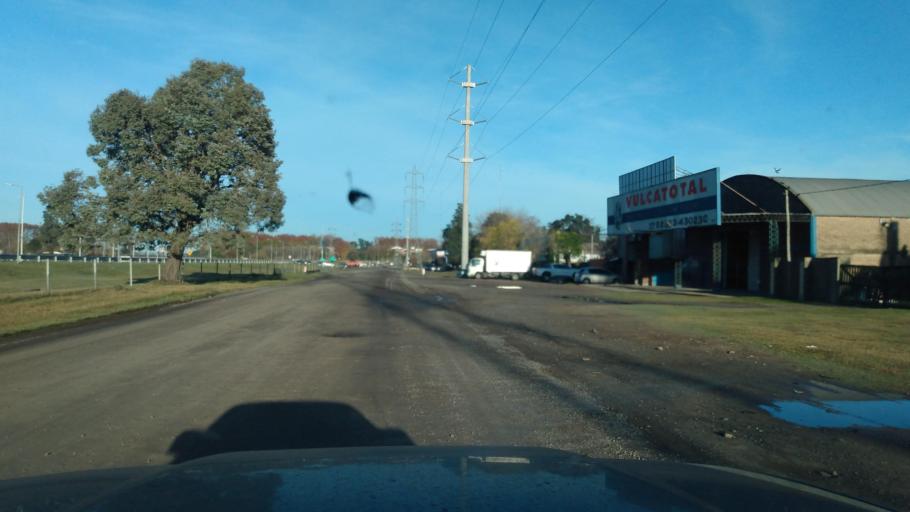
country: AR
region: Buenos Aires
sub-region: Partido de Lujan
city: Lujan
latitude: -34.5752
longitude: -59.0802
